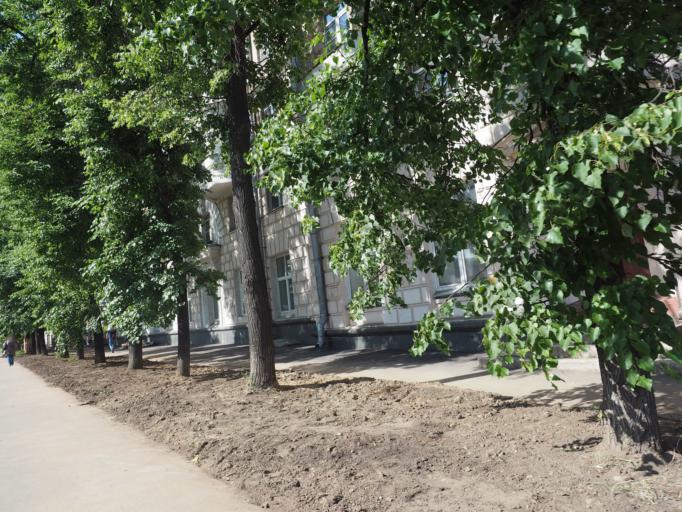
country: RU
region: Moskovskaya
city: Bogorodskoye
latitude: 55.7826
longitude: 37.7425
